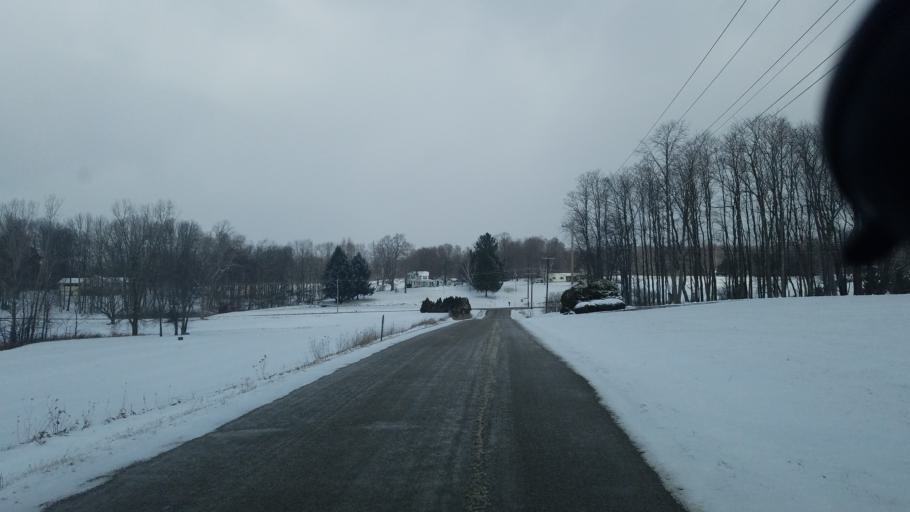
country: US
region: Ohio
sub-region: Richland County
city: Lexington
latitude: 40.6426
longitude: -82.6097
